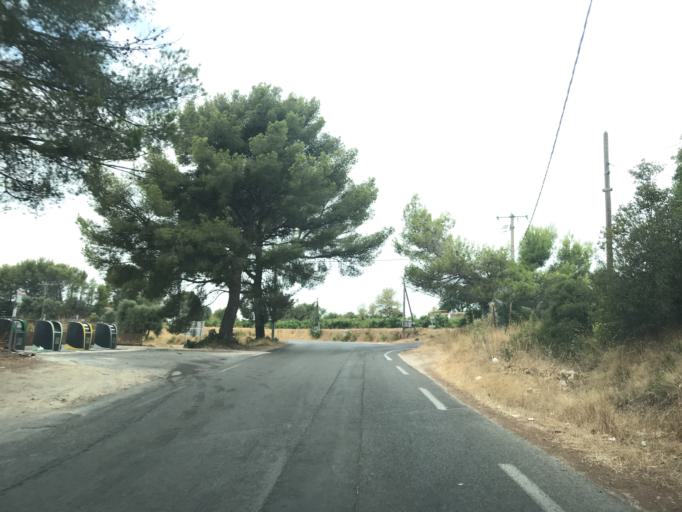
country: FR
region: Provence-Alpes-Cote d'Azur
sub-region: Departement du Var
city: Le Castellet
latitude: 43.1899
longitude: 5.7475
